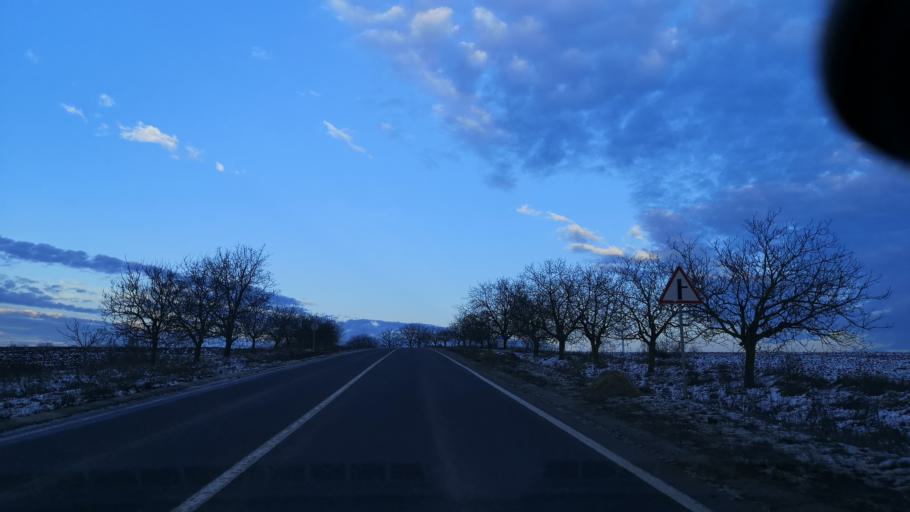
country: MD
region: Orhei
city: Orhei
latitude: 47.5737
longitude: 28.7994
